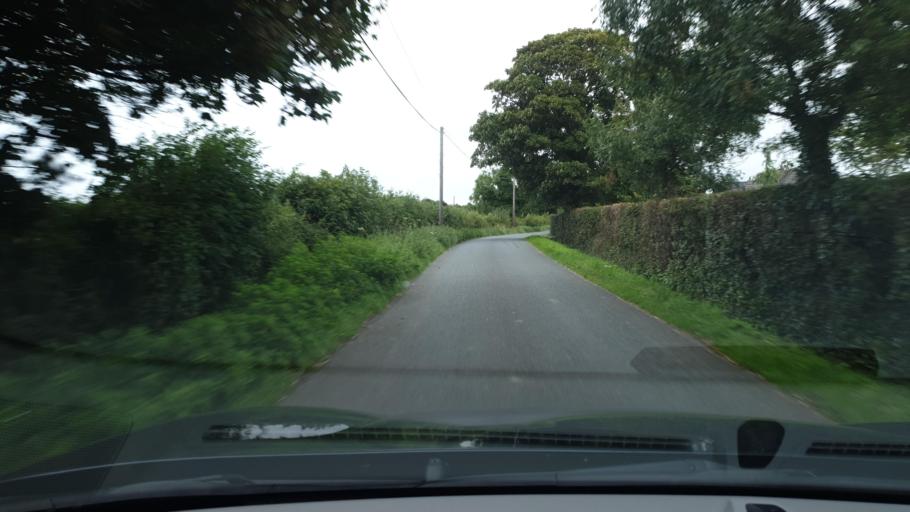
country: IE
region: Leinster
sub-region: An Mhi
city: Ratoath
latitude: 53.5074
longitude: -6.4873
